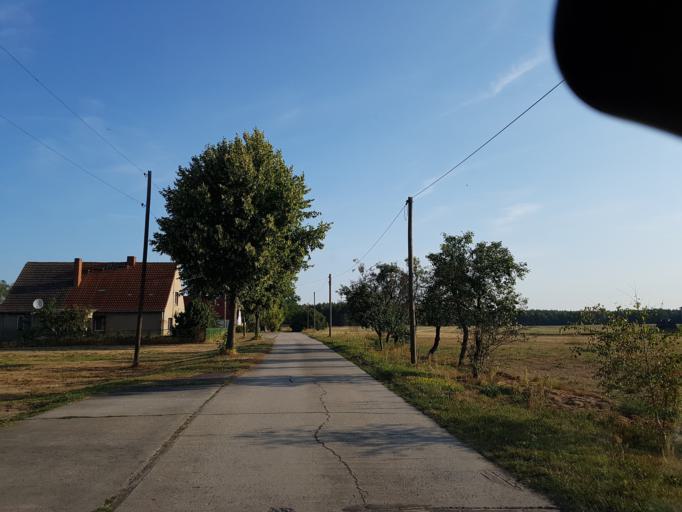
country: DE
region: Brandenburg
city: Niedergorsdorf
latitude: 52.0130
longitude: 12.9251
